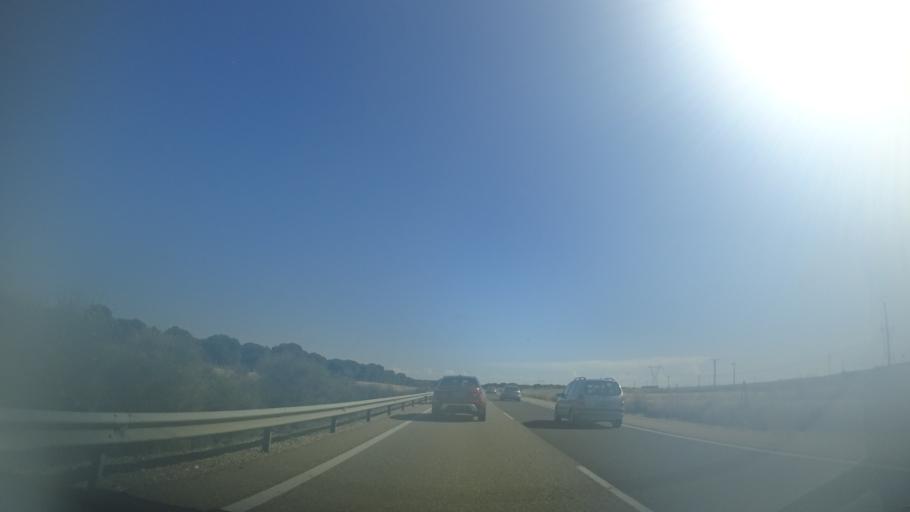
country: ES
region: Castille and Leon
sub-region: Provincia de Valladolid
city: Tordesillas
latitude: 41.4614
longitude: -4.9845
